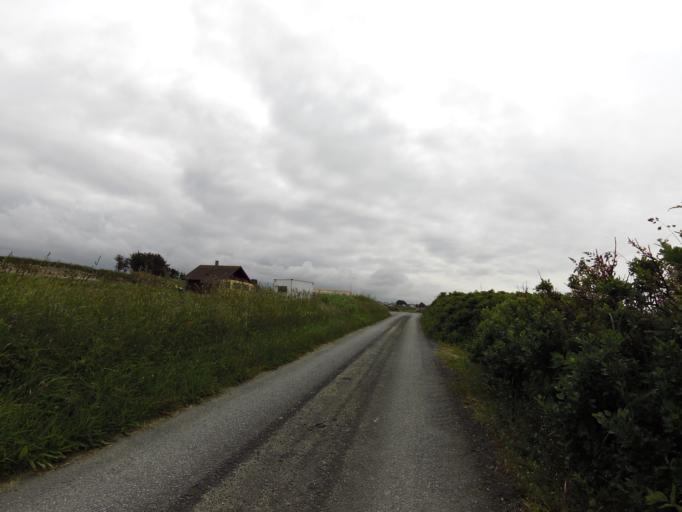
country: NO
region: Rogaland
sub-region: Klepp
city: Kleppe
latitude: 58.8141
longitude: 5.5491
